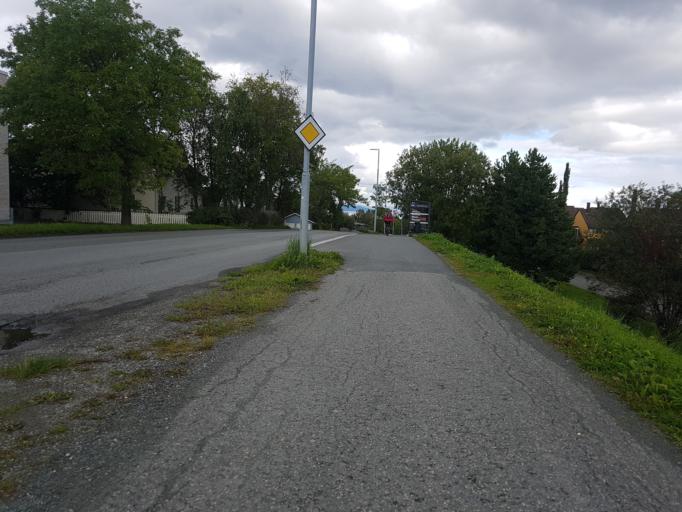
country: NO
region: Sor-Trondelag
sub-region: Trondheim
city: Trondheim
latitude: 63.4158
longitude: 10.4461
